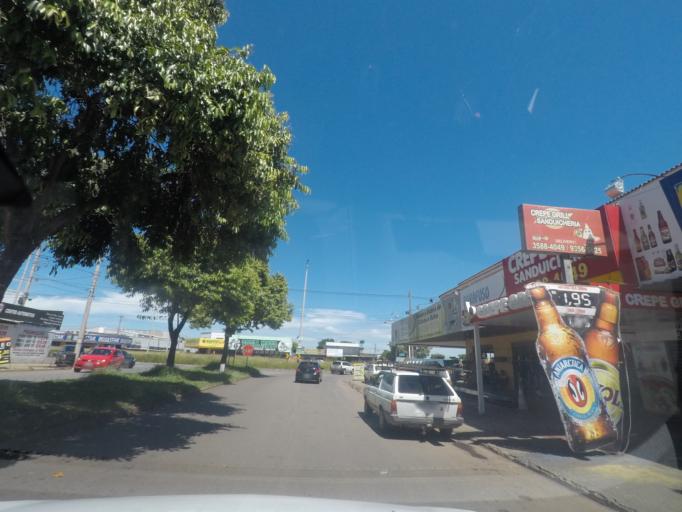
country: BR
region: Goias
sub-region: Aparecida De Goiania
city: Aparecida de Goiania
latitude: -16.7680
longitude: -49.3501
